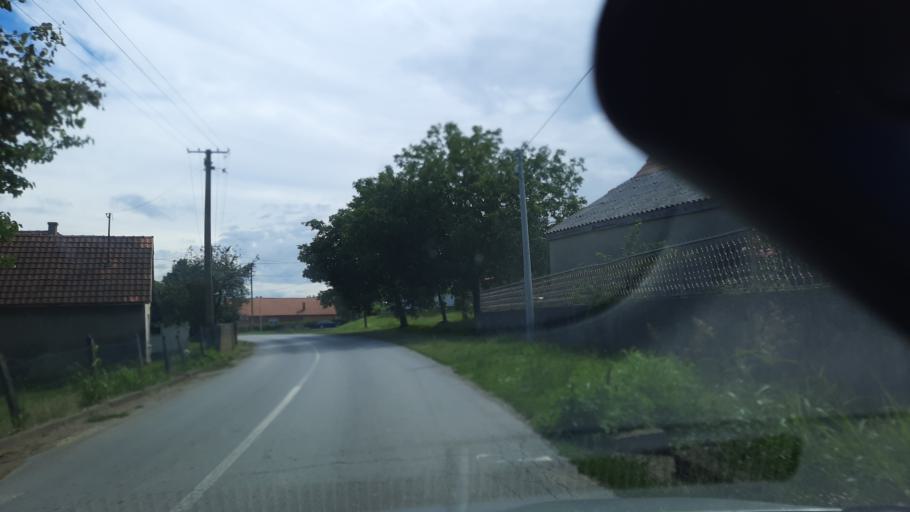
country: RS
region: Autonomna Pokrajina Vojvodina
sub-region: Sremski Okrug
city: Sremska Mitrovica
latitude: 45.1179
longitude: 19.5663
